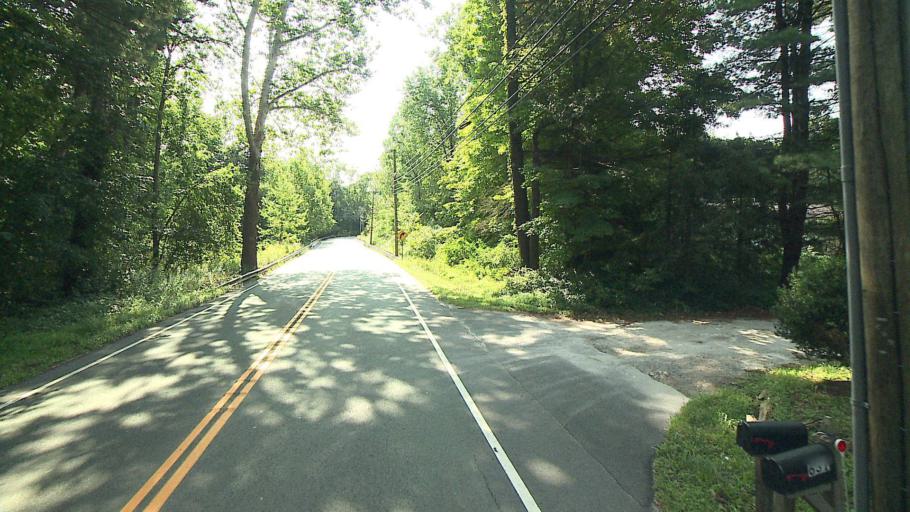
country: US
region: Connecticut
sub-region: Fairfield County
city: Sherman
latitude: 41.6375
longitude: -73.4785
